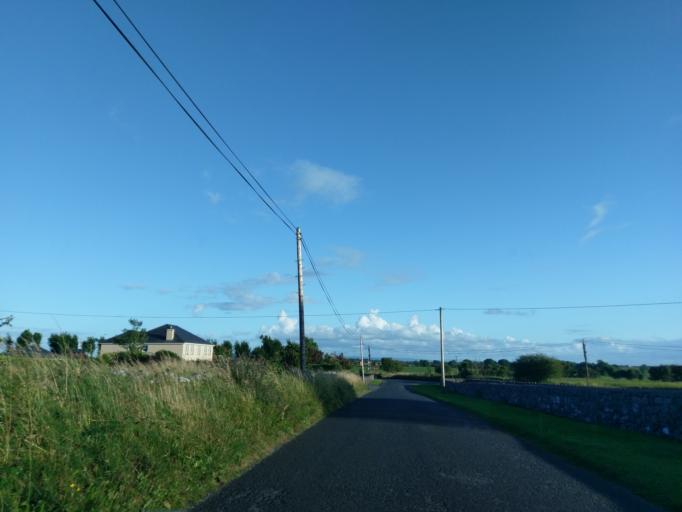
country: IE
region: Connaught
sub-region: County Galway
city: Athenry
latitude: 53.3828
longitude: -8.7187
